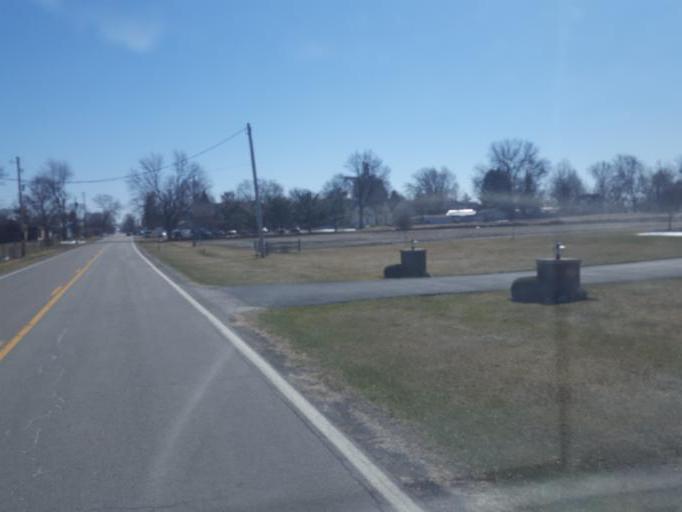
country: US
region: Ohio
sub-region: Wyandot County
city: Upper Sandusky
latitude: 40.7381
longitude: -83.2560
